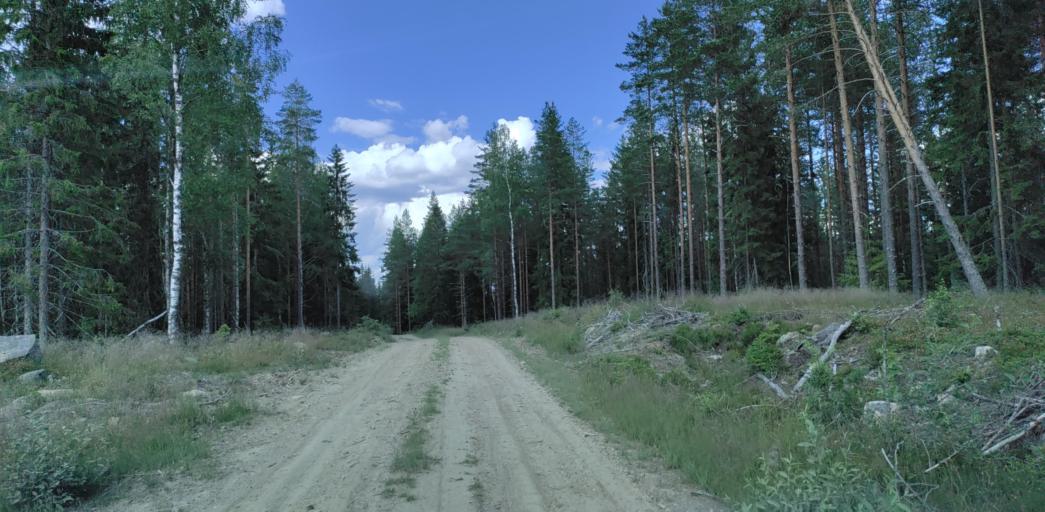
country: SE
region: Vaermland
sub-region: Hagfors Kommun
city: Ekshaerad
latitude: 60.0733
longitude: 13.3458
